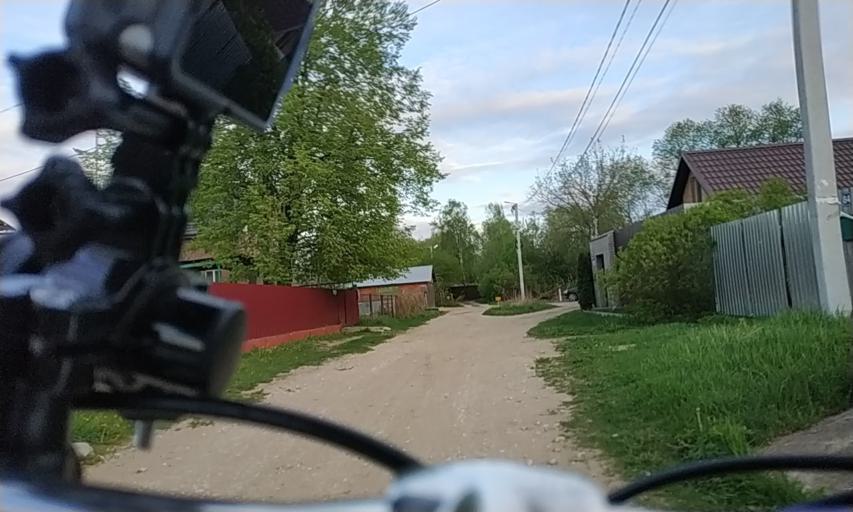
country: RU
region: Moskovskaya
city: Ramenskoye
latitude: 55.5695
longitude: 38.2921
